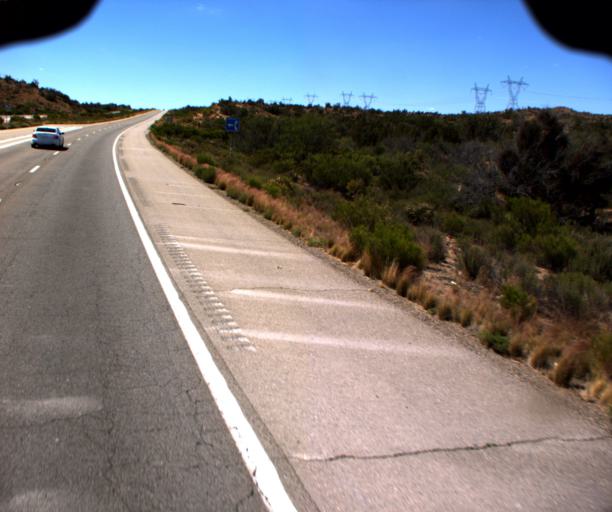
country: US
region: Arizona
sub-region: Yavapai County
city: Bagdad
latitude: 34.4674
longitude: -113.3096
